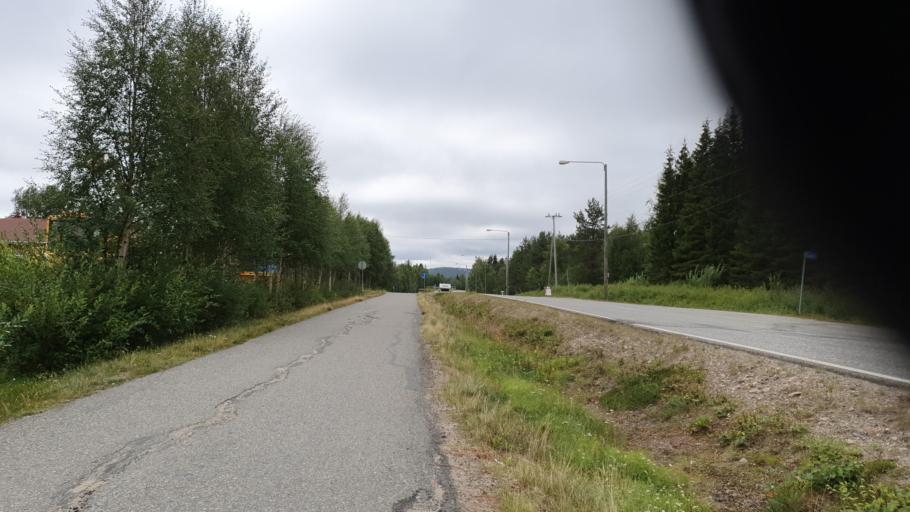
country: FI
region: Lapland
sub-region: Tunturi-Lappi
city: Kolari
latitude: 67.6179
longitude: 24.1531
